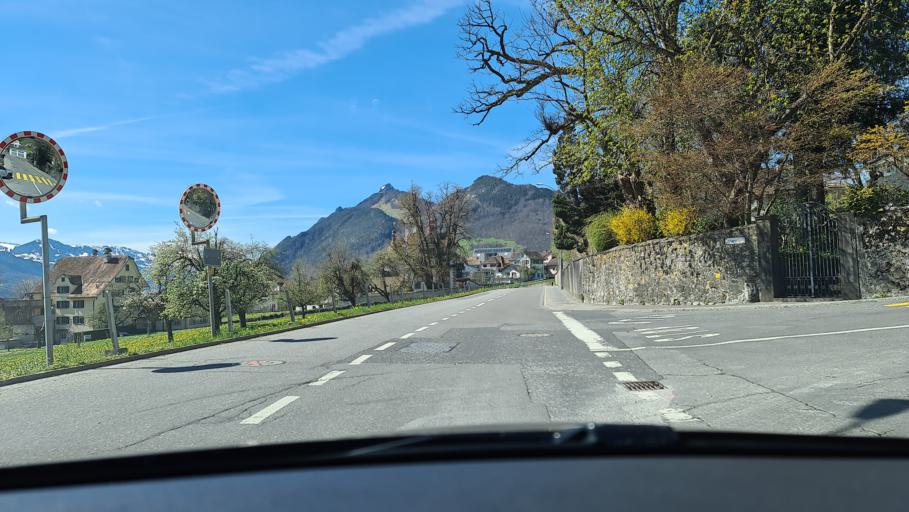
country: CH
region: Schwyz
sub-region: Bezirk Schwyz
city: Schwyz
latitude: 47.0218
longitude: 8.6586
